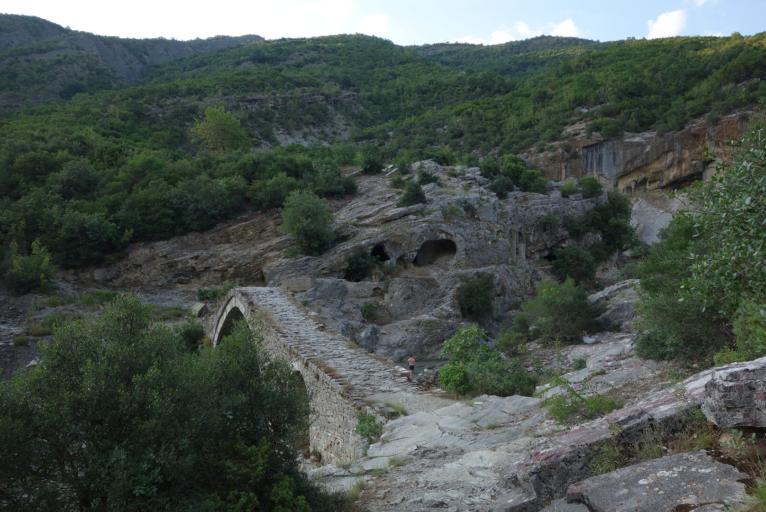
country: AL
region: Gjirokaster
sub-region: Rrethi i Permetit
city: Petran
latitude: 40.2441
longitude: 20.4326
